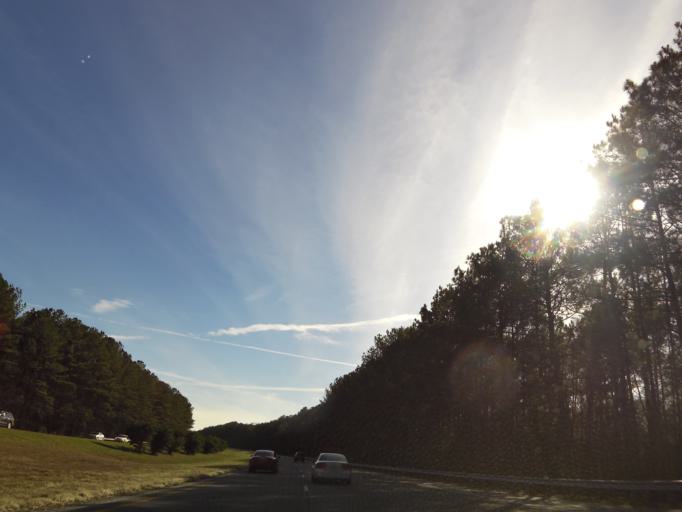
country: US
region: Georgia
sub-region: Harris County
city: Hamilton
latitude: 32.7415
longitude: -85.0194
